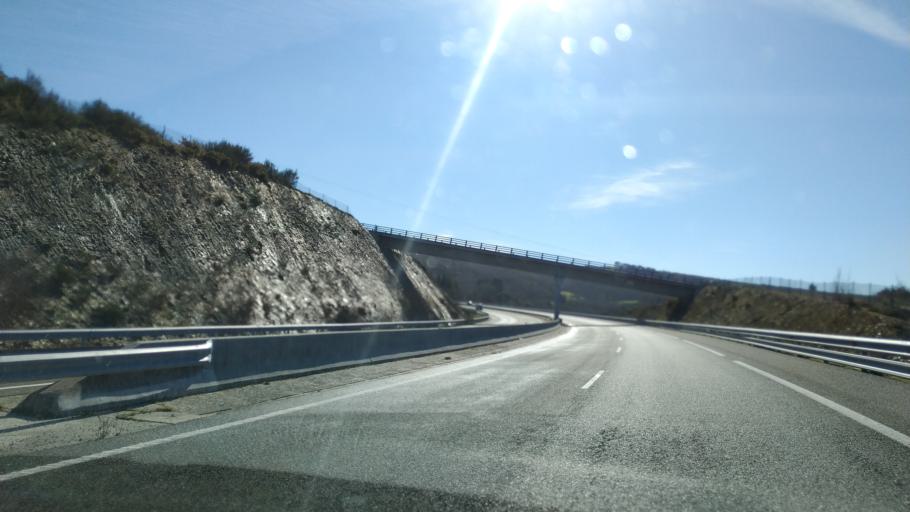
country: ES
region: Galicia
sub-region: Provincia de Pontevedra
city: Dozon
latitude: 42.5726
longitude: -8.0611
